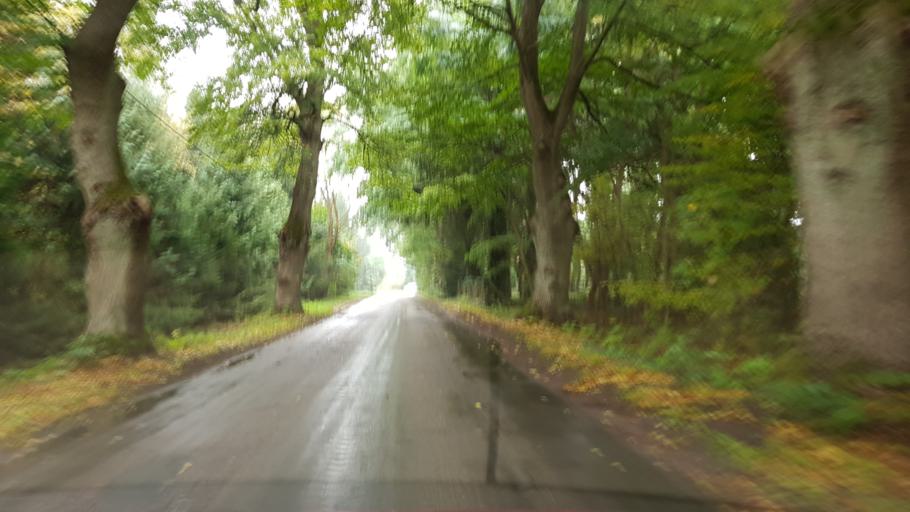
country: PL
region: West Pomeranian Voivodeship
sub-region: Powiat walecki
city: Walcz
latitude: 53.3766
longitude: 16.5029
